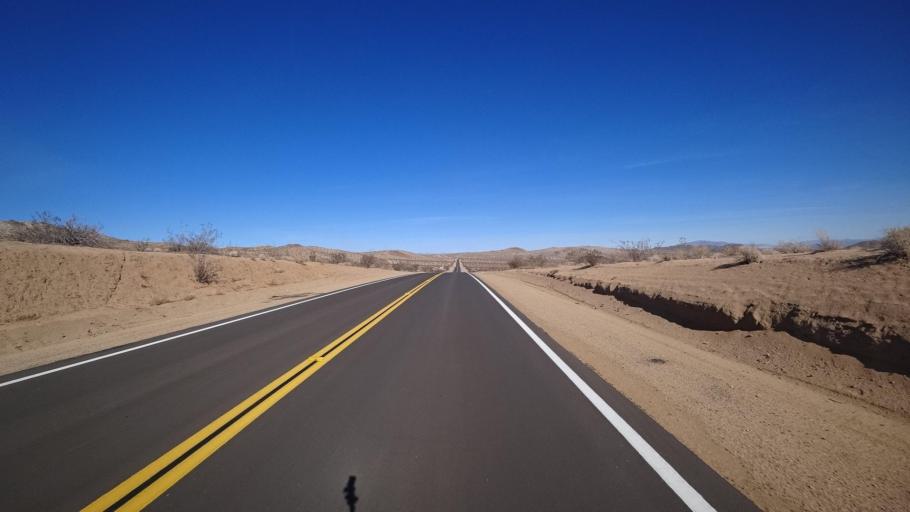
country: US
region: California
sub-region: Kern County
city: Ridgecrest
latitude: 35.5311
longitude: -117.5929
